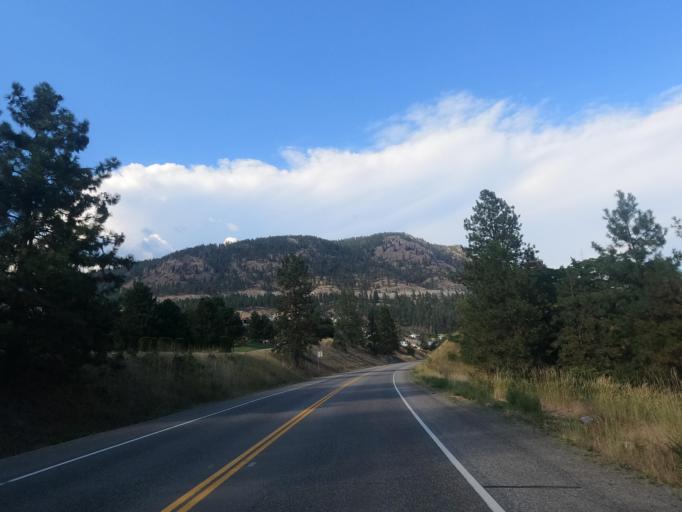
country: CA
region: British Columbia
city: Peachland
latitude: 49.7911
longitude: -119.7063
